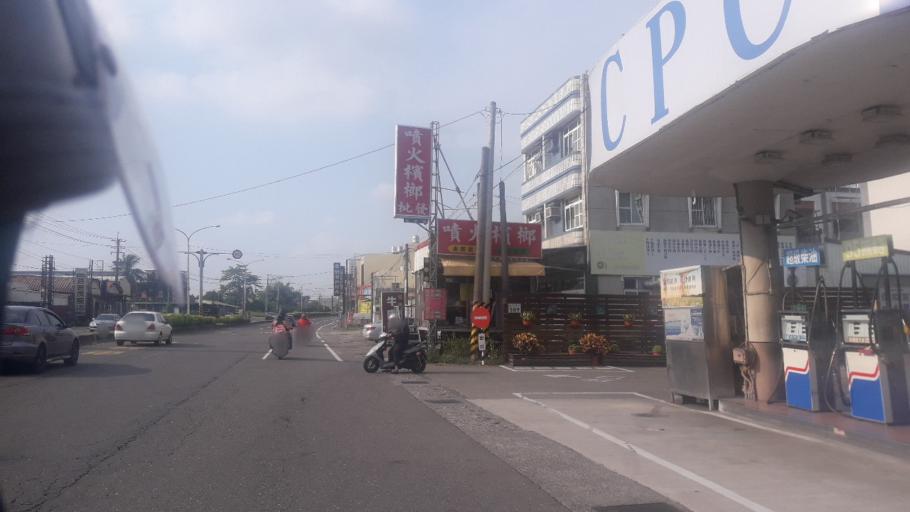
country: TW
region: Taiwan
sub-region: Tainan
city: Tainan
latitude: 22.8661
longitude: 120.2566
